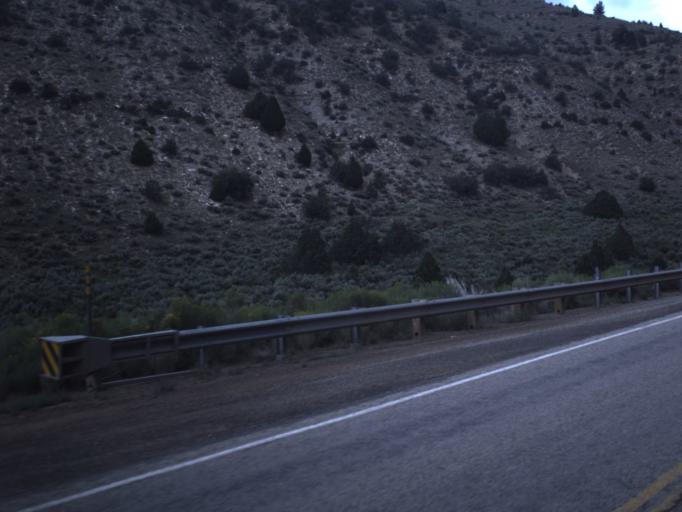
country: US
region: Utah
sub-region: Carbon County
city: Helper
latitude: 39.8360
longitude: -110.7842
